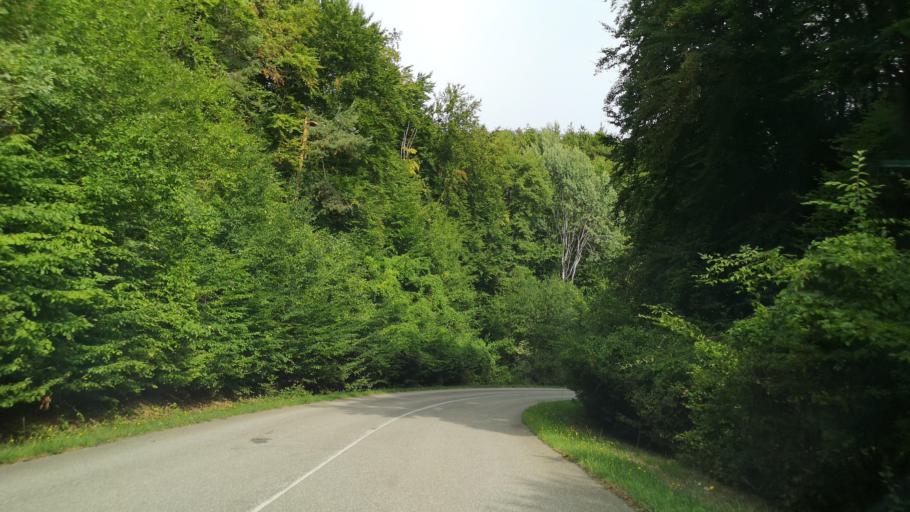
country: SK
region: Banskobystricky
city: Revuca
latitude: 48.5751
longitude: 20.0351
